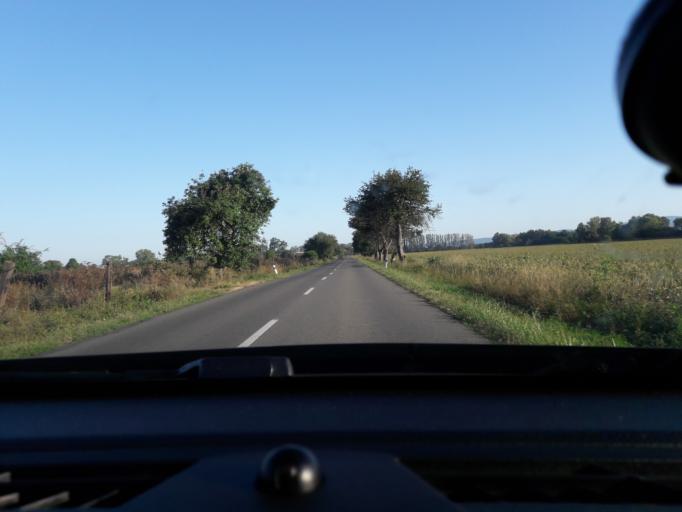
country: SK
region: Kosicky
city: Michalovce
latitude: 48.6887
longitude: 21.9298
